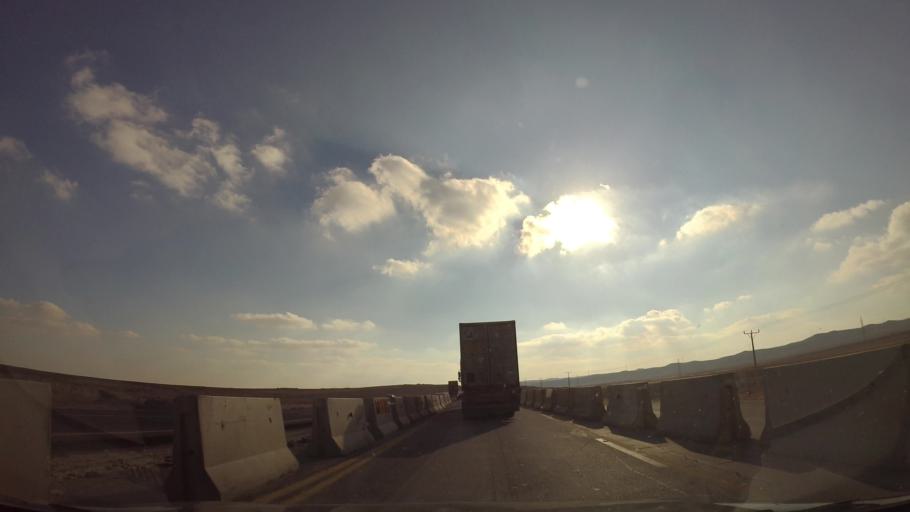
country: JO
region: Karak
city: Karak City
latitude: 31.1299
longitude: 36.0235
